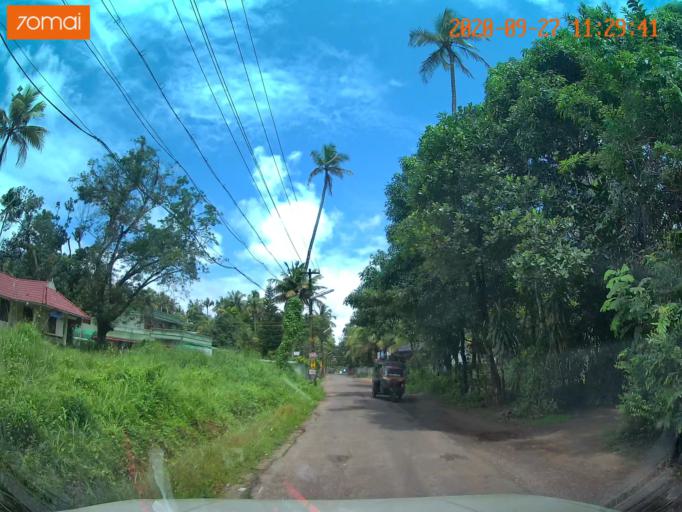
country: IN
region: Kerala
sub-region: Thrissur District
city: Thanniyam
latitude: 10.4168
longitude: 76.1349
